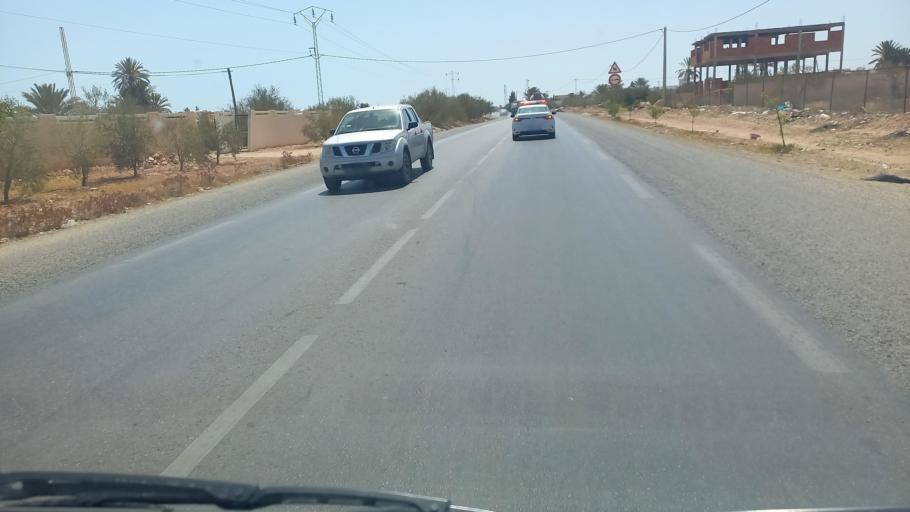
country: TN
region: Madanin
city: Houmt Souk
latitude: 33.8124
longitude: 10.8772
